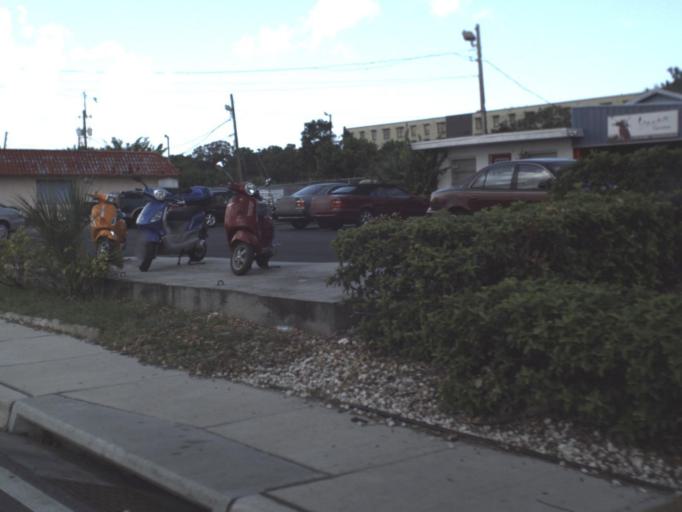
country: US
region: Florida
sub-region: Pinellas County
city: Clearwater
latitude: 27.9591
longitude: -82.7877
